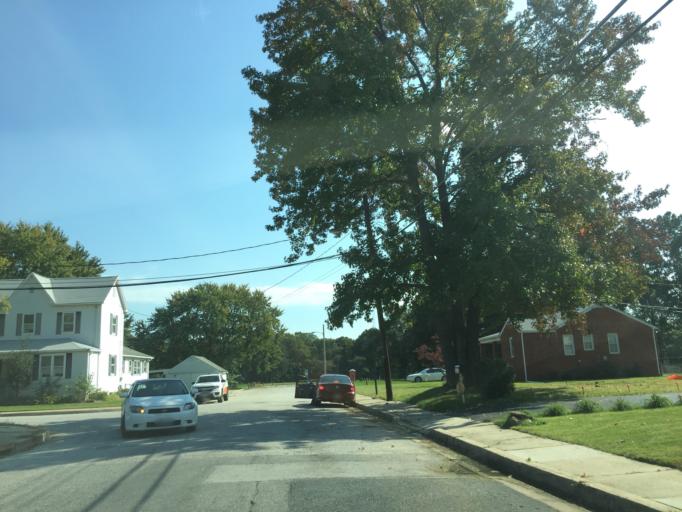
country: US
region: Maryland
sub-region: Baltimore County
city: Essex
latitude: 39.3074
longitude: -76.4574
